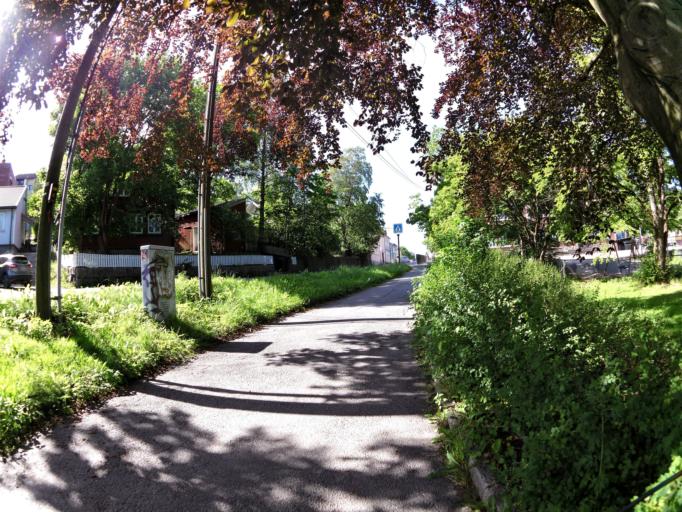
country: NO
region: Ostfold
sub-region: Fredrikstad
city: Fredrikstad
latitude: 59.2182
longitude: 10.9389
